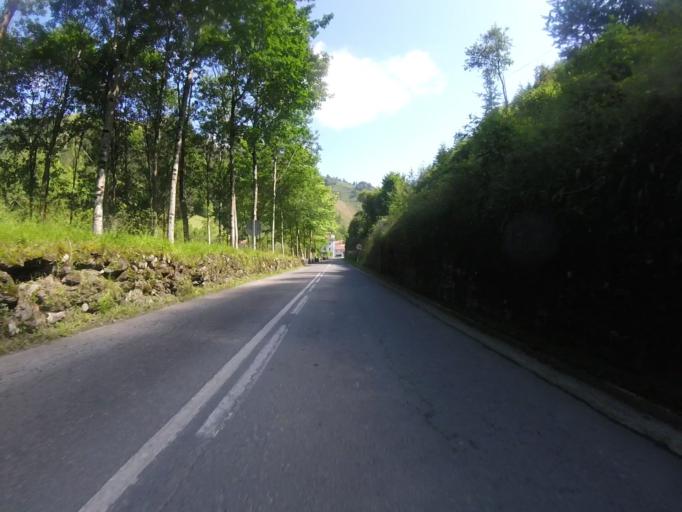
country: ES
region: Basque Country
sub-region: Provincia de Guipuzcoa
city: Beizama
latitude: 43.1061
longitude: -2.2419
